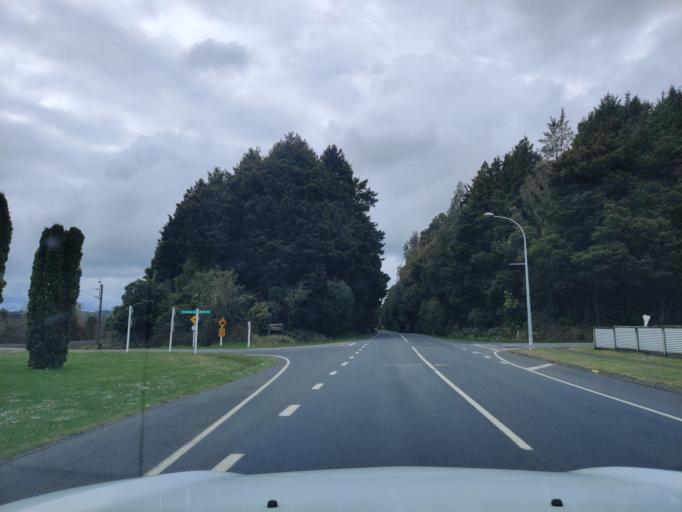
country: NZ
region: Waikato
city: Turangi
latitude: -38.9969
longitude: 175.3779
